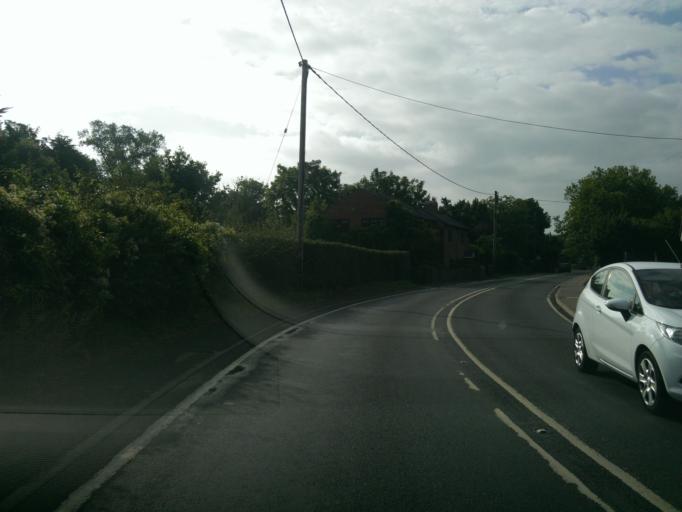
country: GB
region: England
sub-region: Essex
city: Little Clacton
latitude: 51.8418
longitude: 1.1289
